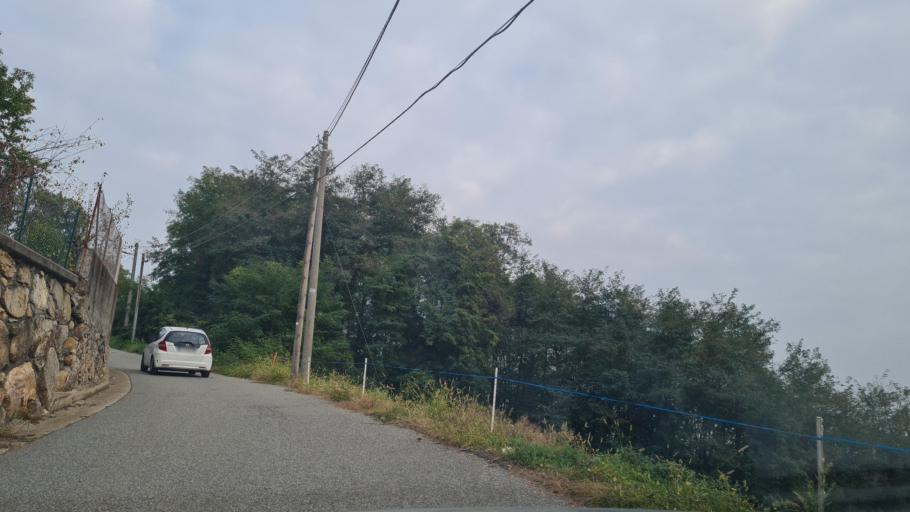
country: IT
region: Piedmont
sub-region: Provincia di Biella
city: Occhieppo Superiore
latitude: 45.5625
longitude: 8.0046
